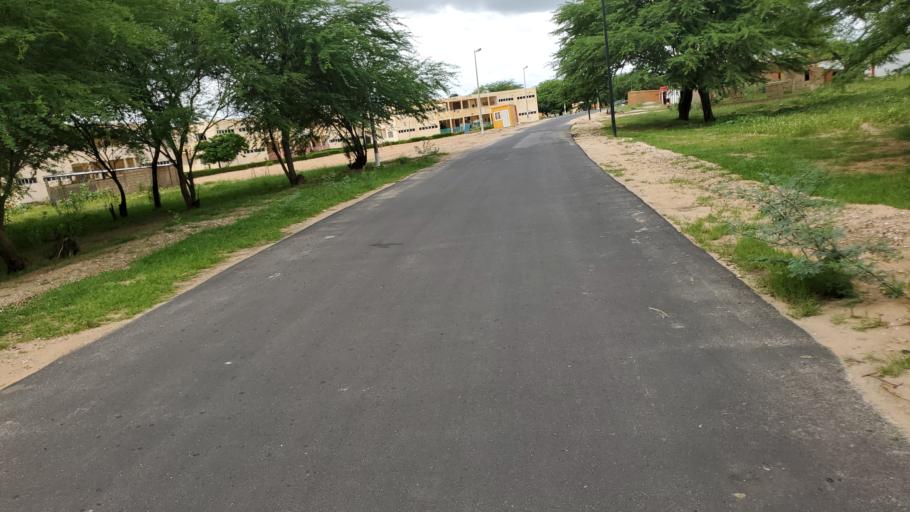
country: SN
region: Saint-Louis
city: Saint-Louis
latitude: 16.0642
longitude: -16.4280
